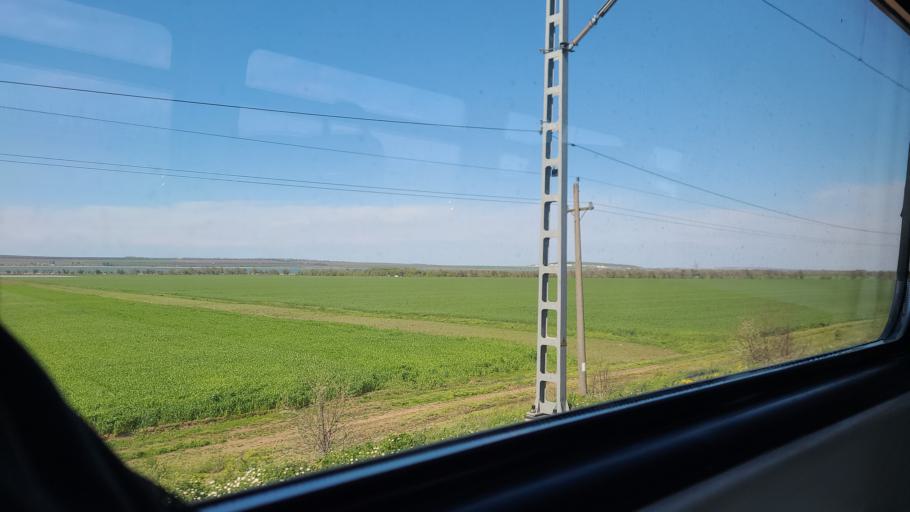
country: RU
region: Krasnodarskiy
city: Starotitarovskaya
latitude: 45.1981
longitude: 37.2057
